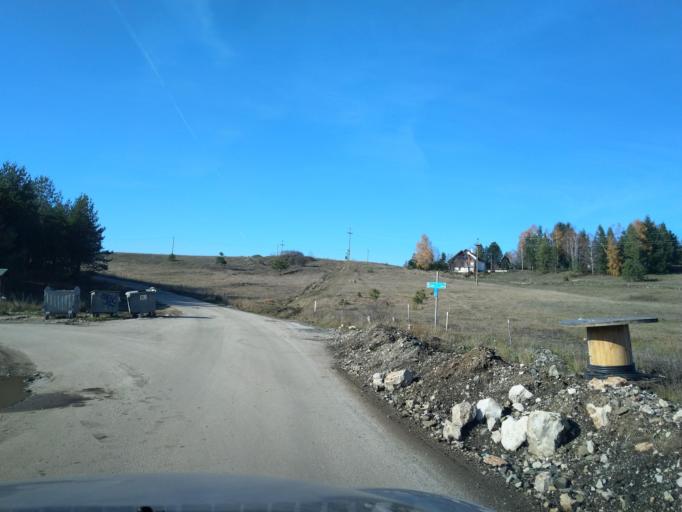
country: RS
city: Zlatibor
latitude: 43.7345
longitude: 19.6806
